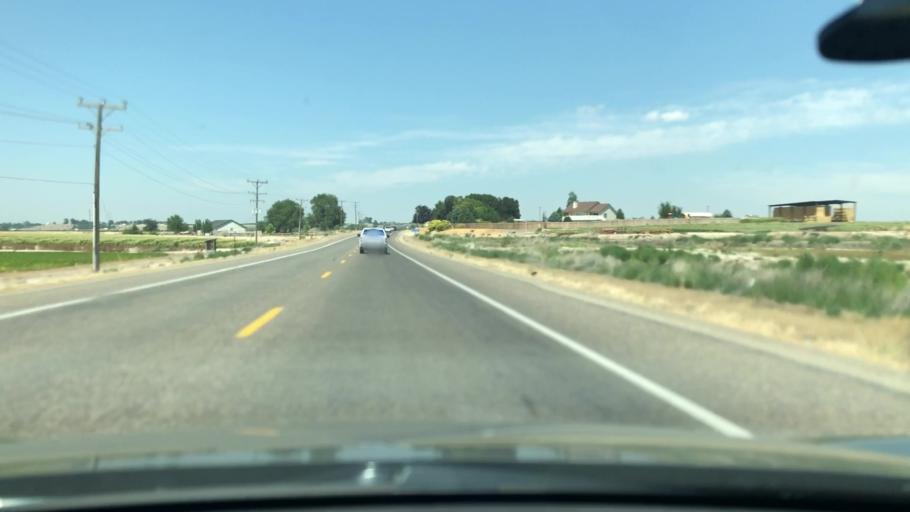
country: US
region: Idaho
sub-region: Owyhee County
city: Homedale
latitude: 43.6359
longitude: -116.9117
